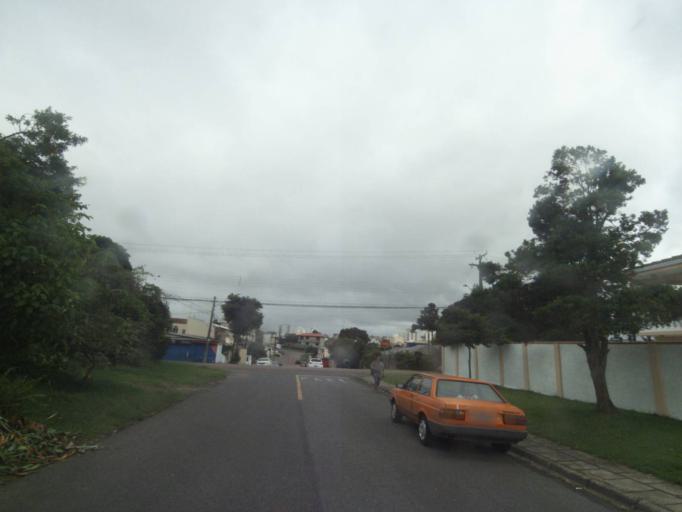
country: BR
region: Parana
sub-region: Curitiba
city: Curitiba
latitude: -25.4906
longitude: -49.2827
